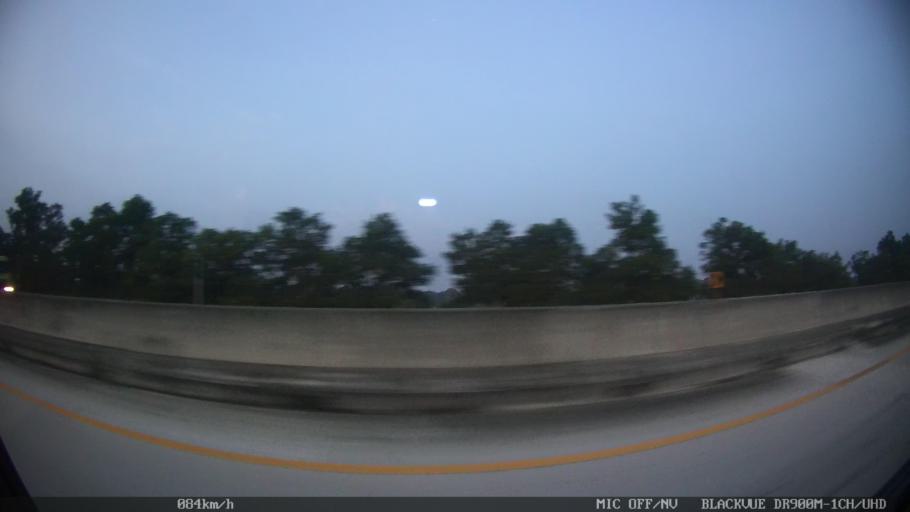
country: ID
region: Lampung
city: Sidorejo
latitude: -5.5683
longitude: 105.5367
